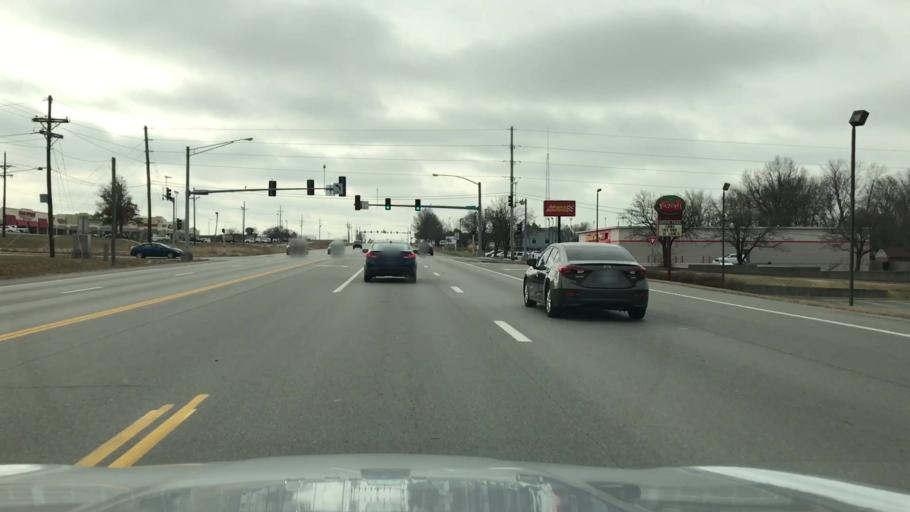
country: US
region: Missouri
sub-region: Jackson County
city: Lees Summit
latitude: 38.9109
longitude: -94.3626
